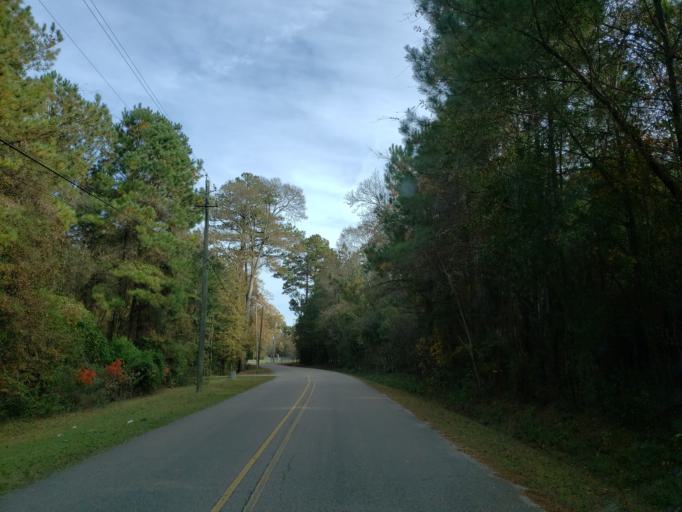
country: US
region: Mississippi
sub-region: Forrest County
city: Glendale
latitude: 31.3542
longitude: -89.3335
